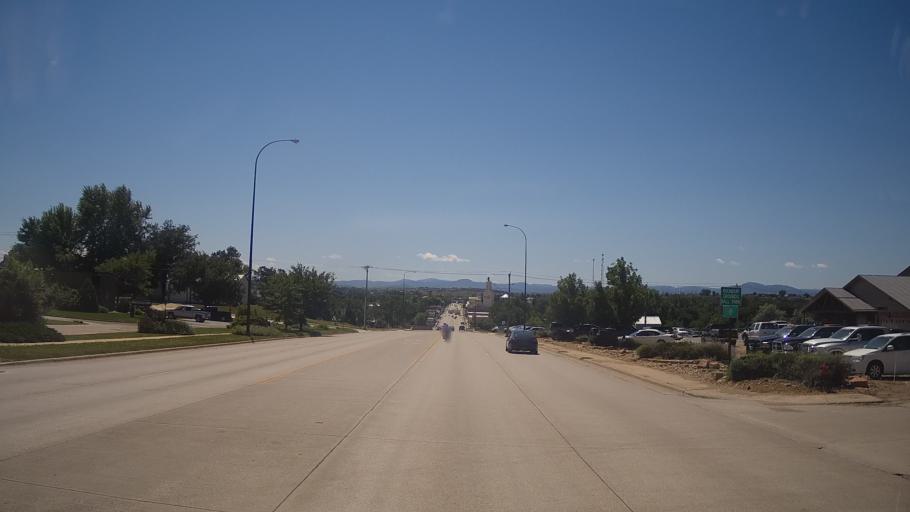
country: US
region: South Dakota
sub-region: Butte County
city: Belle Fourche
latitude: 44.6782
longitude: -103.8537
